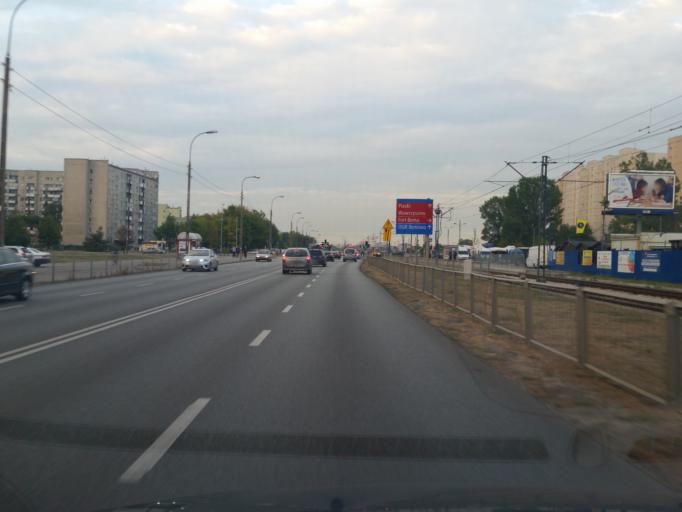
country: PL
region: Masovian Voivodeship
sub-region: Warszawa
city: Bemowo
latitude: 52.2561
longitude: 20.9184
